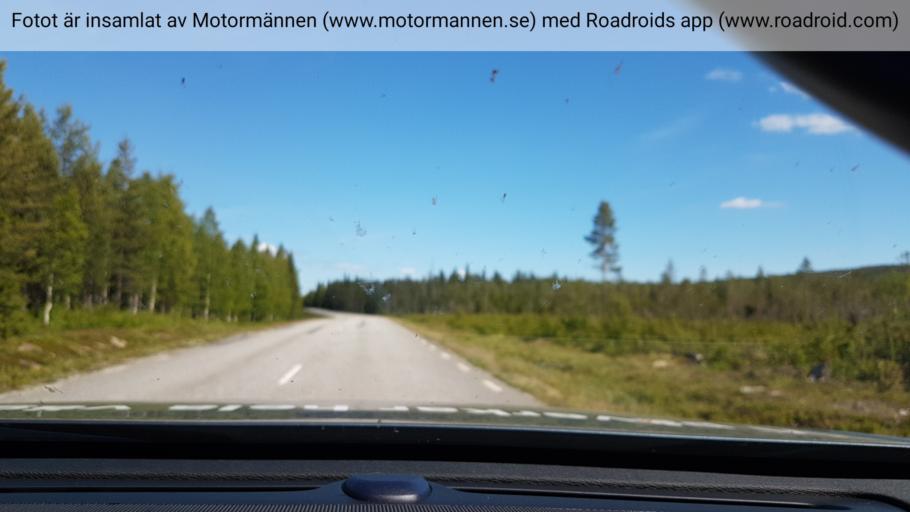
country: SE
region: Vaesterbotten
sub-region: Lycksele Kommun
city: Soderfors
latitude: 64.6236
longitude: 18.1034
